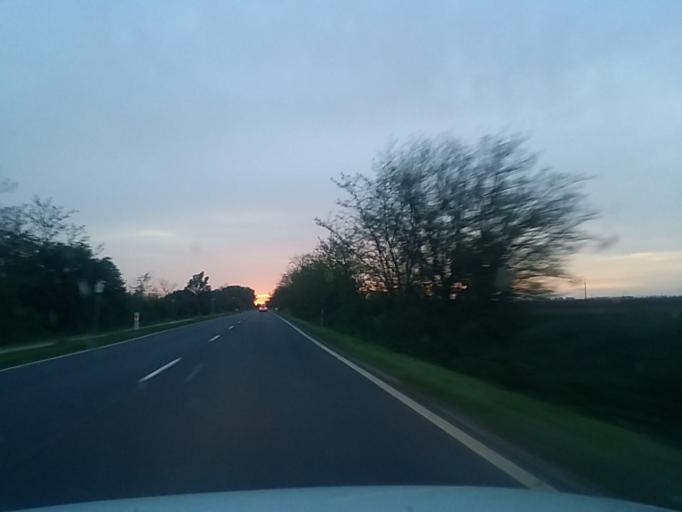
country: HU
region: Bekes
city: Kondoros
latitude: 46.7429
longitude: 20.8710
